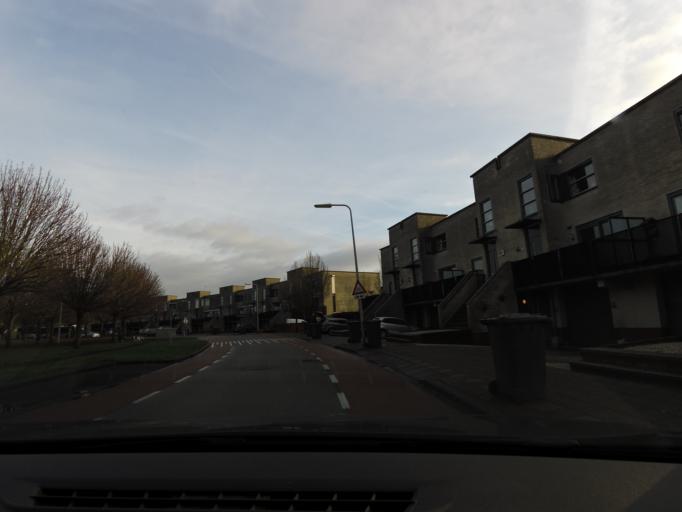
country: NL
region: South Holland
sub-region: Gemeente Hellevoetsluis
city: Nieuwenhoorn
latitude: 51.8445
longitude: 4.1633
